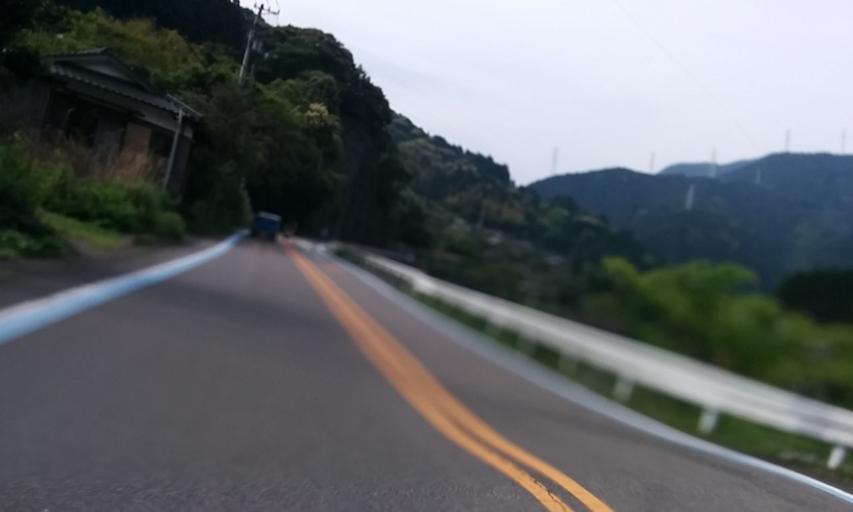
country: JP
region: Ehime
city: Niihama
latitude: 33.9125
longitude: 133.3100
